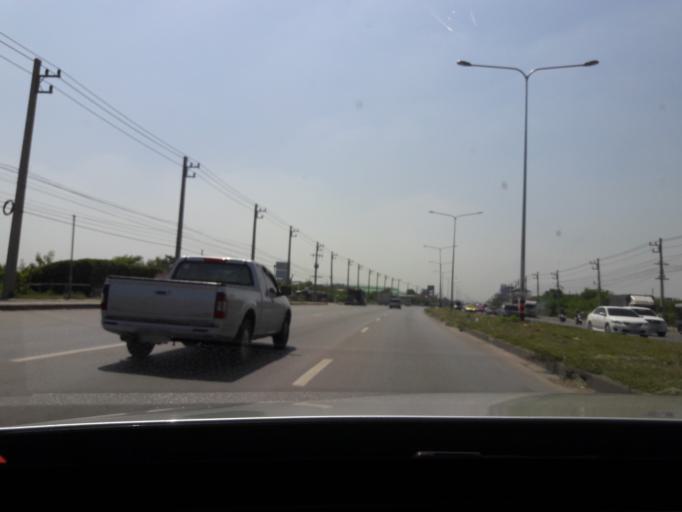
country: TH
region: Samut Sakhon
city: Krathum Baen
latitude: 13.6598
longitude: 100.3119
